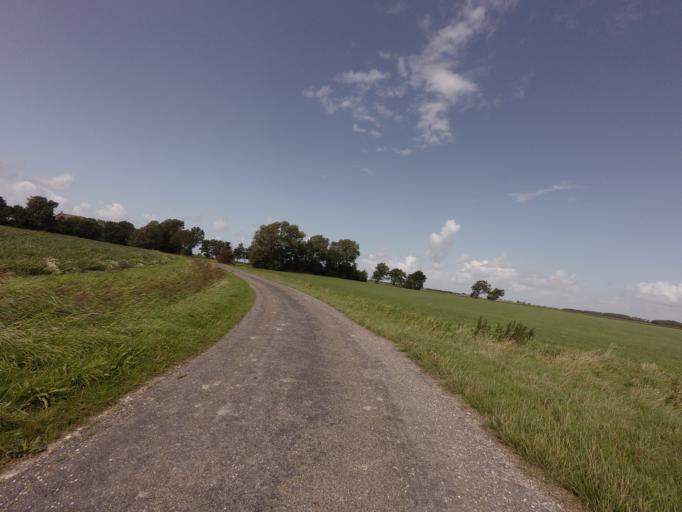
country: NL
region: Friesland
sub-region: Gemeente Harlingen
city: Harlingen
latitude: 53.1217
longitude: 5.4419
